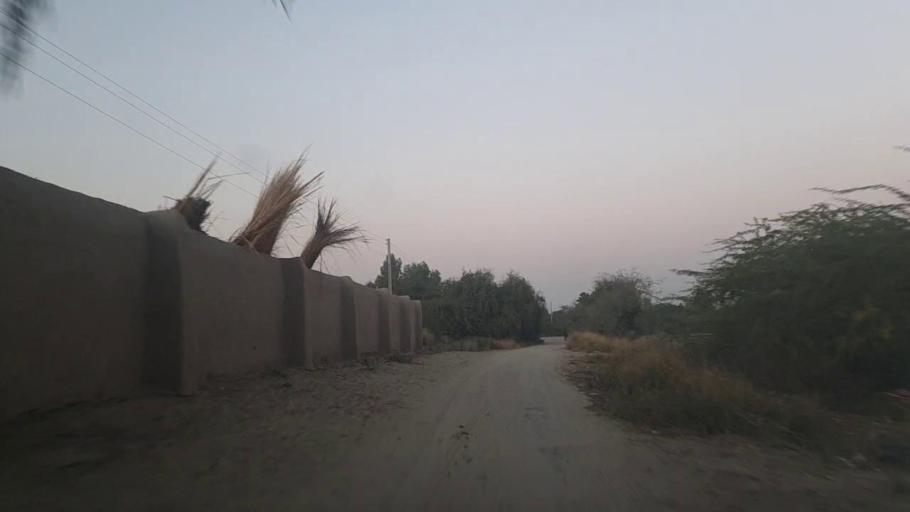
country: PK
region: Sindh
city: Jam Sahib
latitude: 26.3876
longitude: 68.8179
